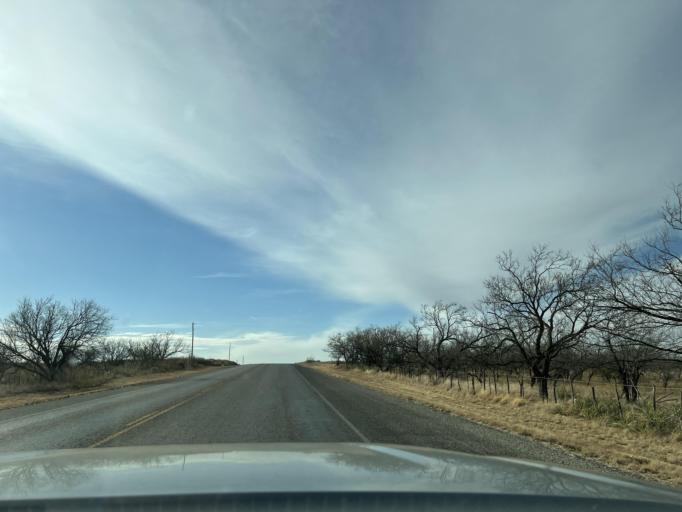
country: US
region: Texas
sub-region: Fisher County
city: Rotan
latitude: 32.7395
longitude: -100.5247
